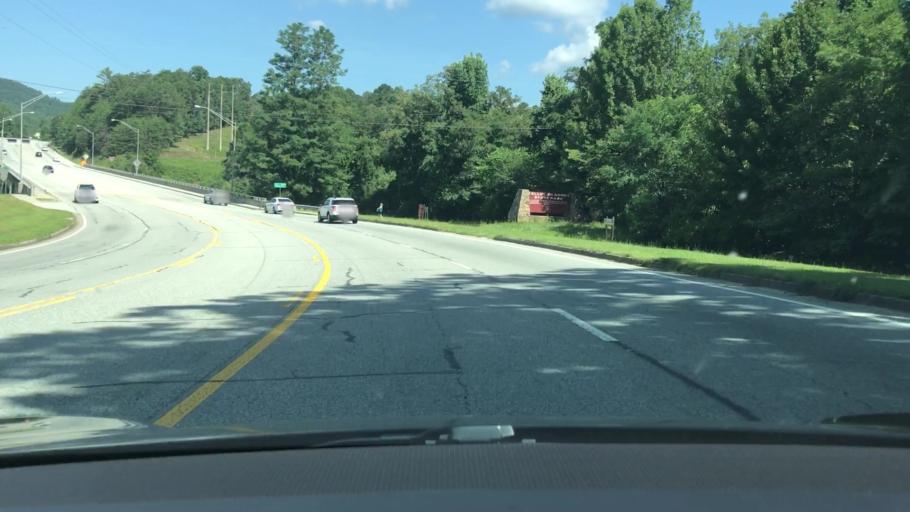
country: US
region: Georgia
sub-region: Rabun County
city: Clayton
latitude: 34.7383
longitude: -83.3937
